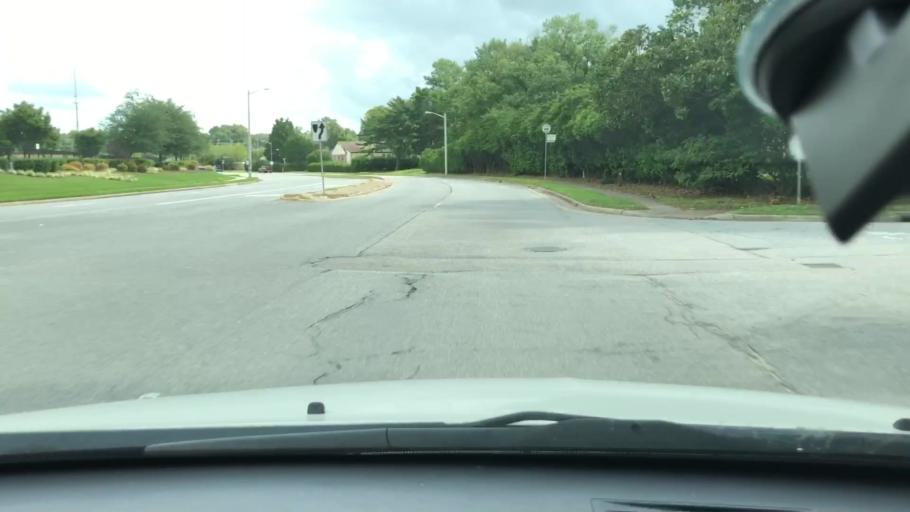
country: US
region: Virginia
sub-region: City of Chesapeake
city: Chesapeake
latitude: 36.8103
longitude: -76.2096
